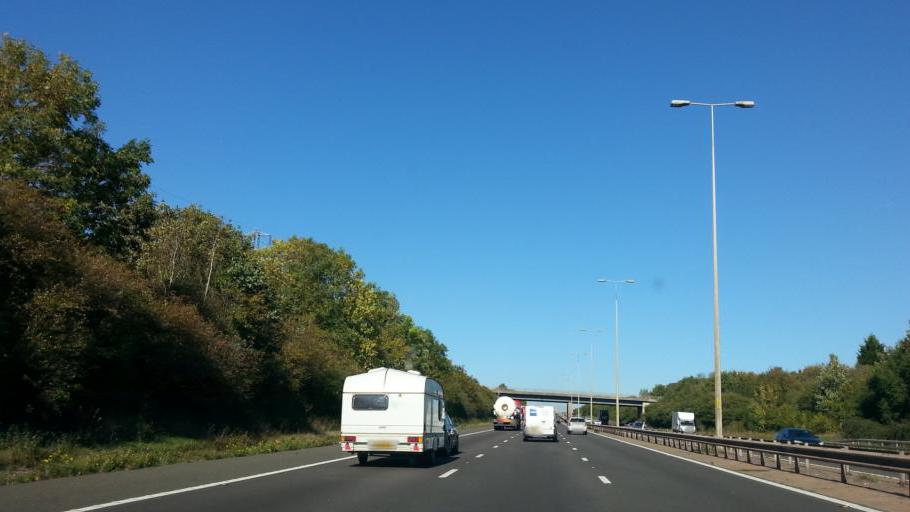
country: GB
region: England
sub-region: Worcestershire
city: Worcester
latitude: 52.1838
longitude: -2.1713
